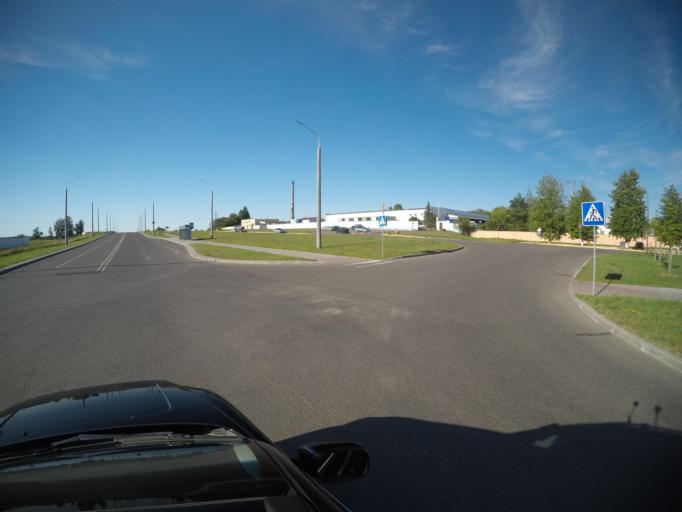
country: BY
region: Grodnenskaya
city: Hrodna
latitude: 53.7148
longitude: 23.8253
